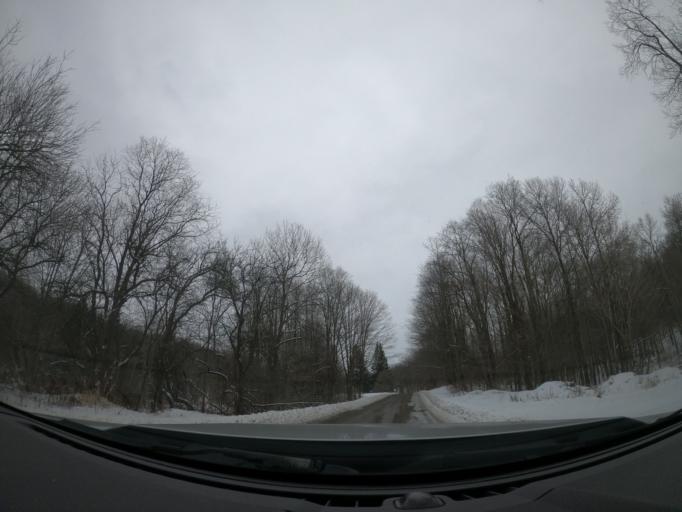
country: US
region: New York
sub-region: Cayuga County
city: Moravia
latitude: 42.7331
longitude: -76.2846
